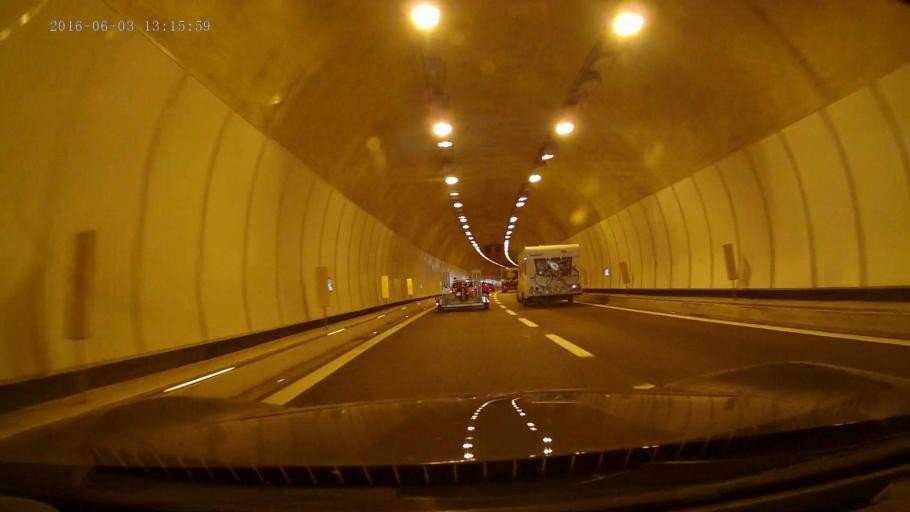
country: IT
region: Trentino-Alto Adige
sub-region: Bolzano
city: Ponte Gardena
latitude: 46.5966
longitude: 11.5331
